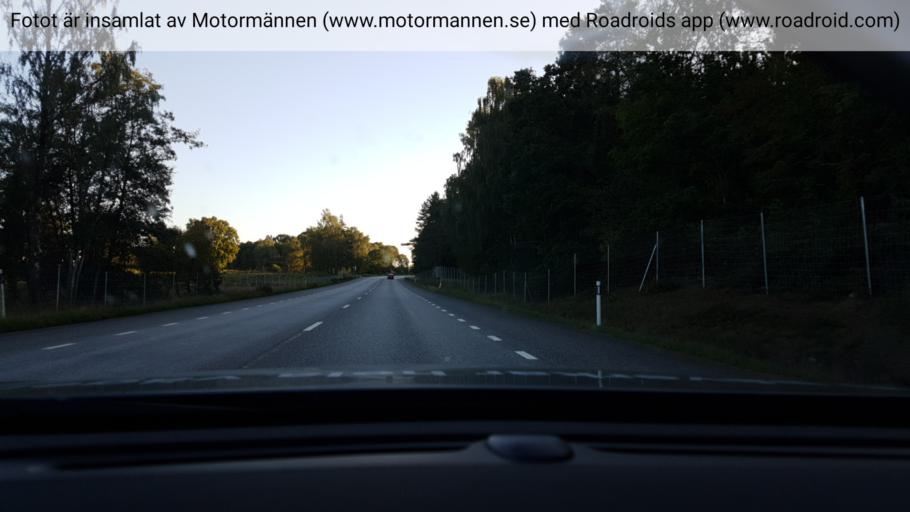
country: SE
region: Halland
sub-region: Halmstads Kommun
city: Aled
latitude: 56.7716
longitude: 12.9501
